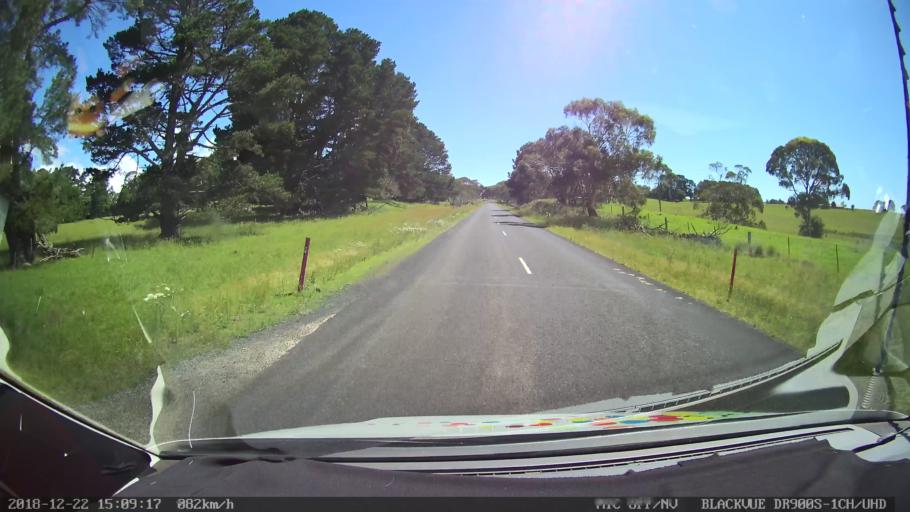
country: AU
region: New South Wales
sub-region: Bellingen
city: Dorrigo
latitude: -30.3227
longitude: 152.4106
